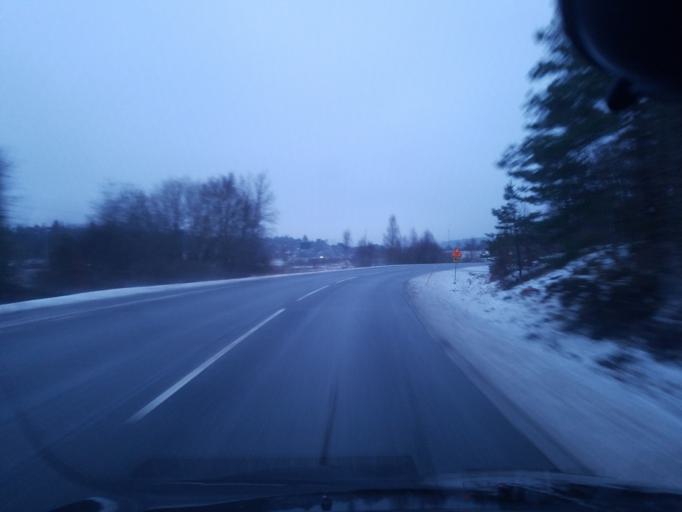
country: SE
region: Vaestra Goetaland
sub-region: Lysekils Kommun
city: Lysekil
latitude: 58.3020
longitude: 11.4763
